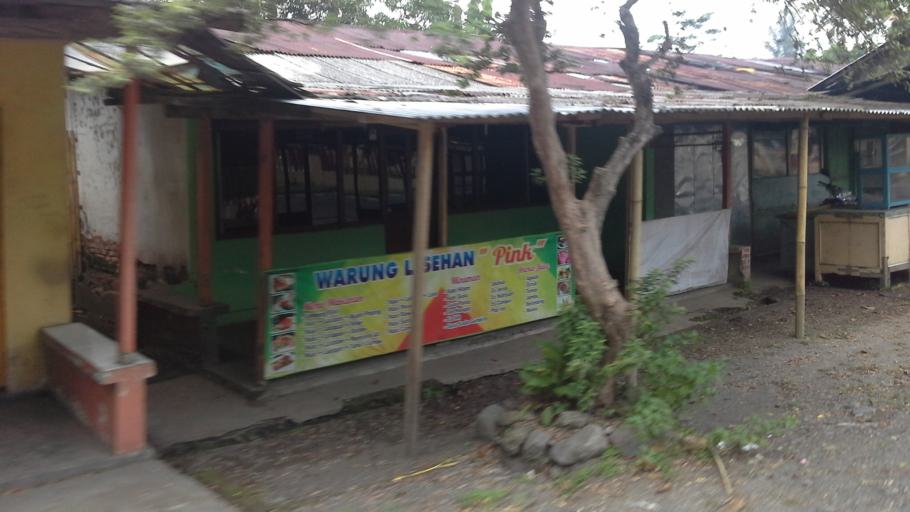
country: ID
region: East Java
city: Bondowoso
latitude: -7.9081
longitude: 113.8542
